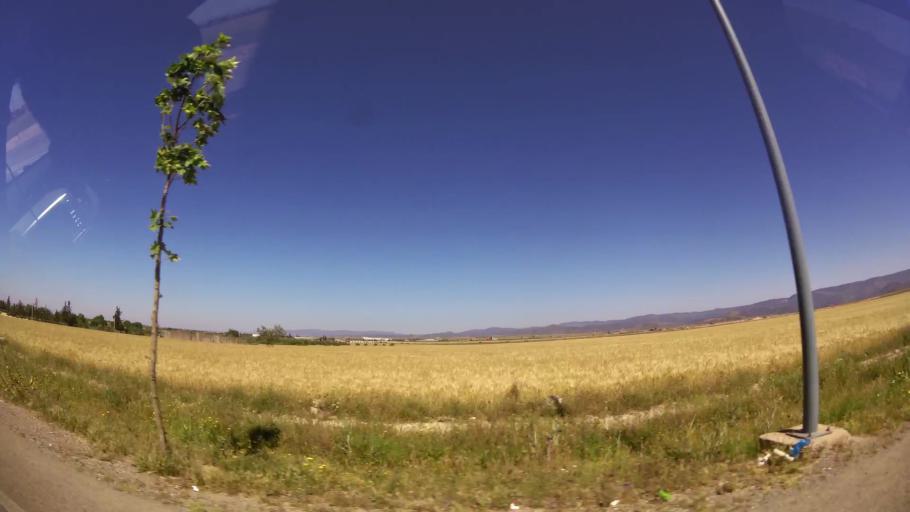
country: MA
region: Oriental
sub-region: Oujda-Angad
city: Oujda
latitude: 34.6902
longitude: -1.8574
